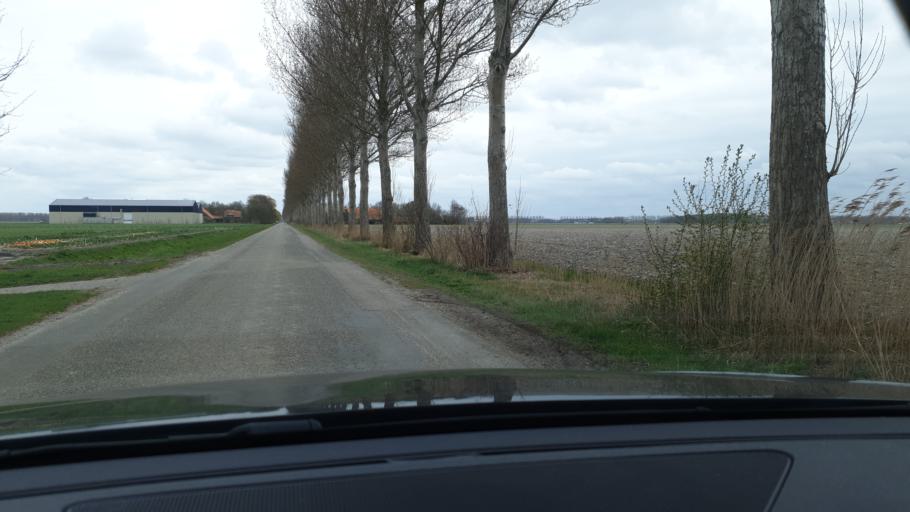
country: NL
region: Flevoland
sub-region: Gemeente Urk
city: Urk
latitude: 52.7393
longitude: 5.6149
